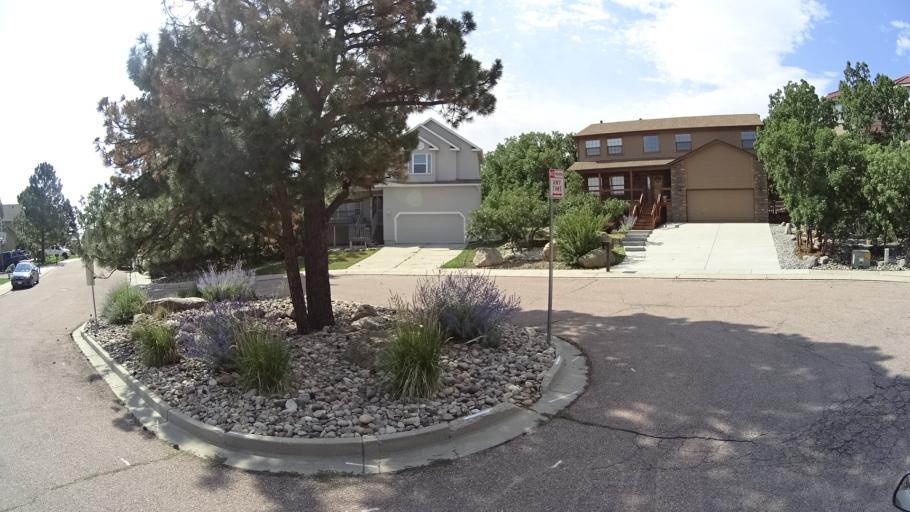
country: US
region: Colorado
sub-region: El Paso County
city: Fort Carson
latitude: 38.7579
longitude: -104.8301
